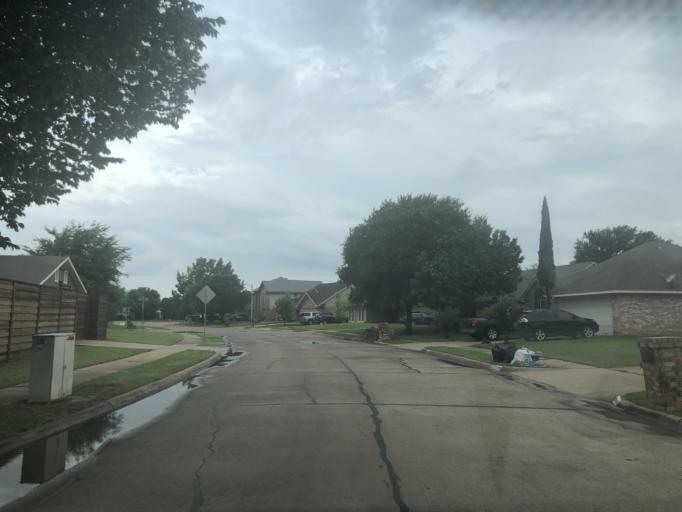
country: US
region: Texas
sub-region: Dallas County
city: Irving
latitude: 32.7868
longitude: -96.9626
